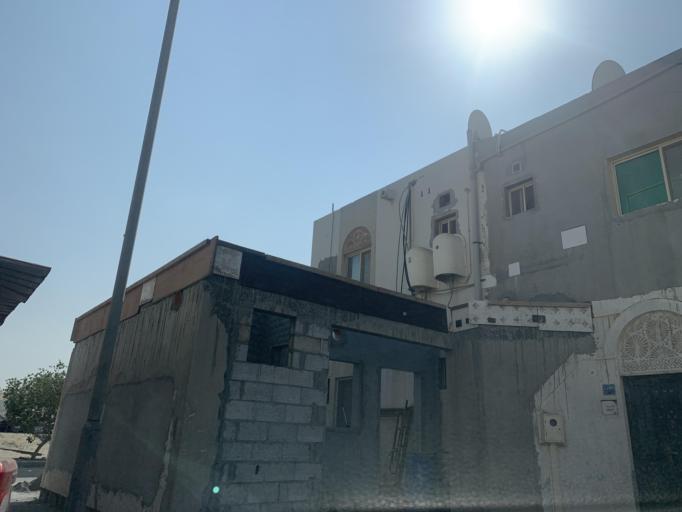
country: BH
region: Central Governorate
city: Madinat Hamad
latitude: 26.1231
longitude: 50.4940
